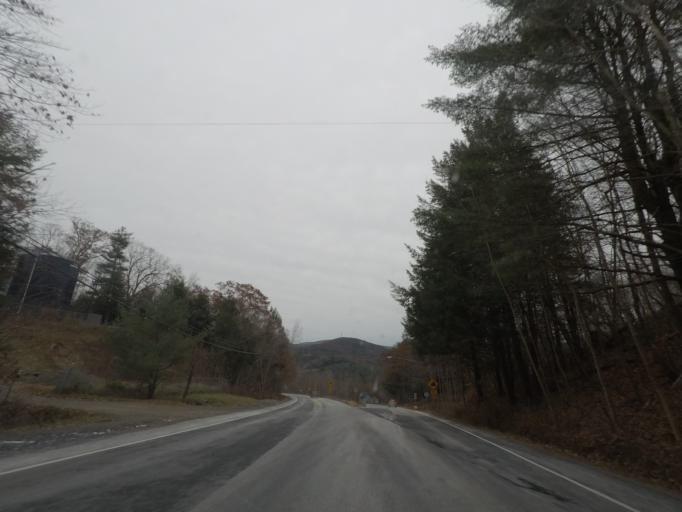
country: US
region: New York
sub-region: Rensselaer County
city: Hoosick Falls
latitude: 42.7525
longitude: -73.3513
